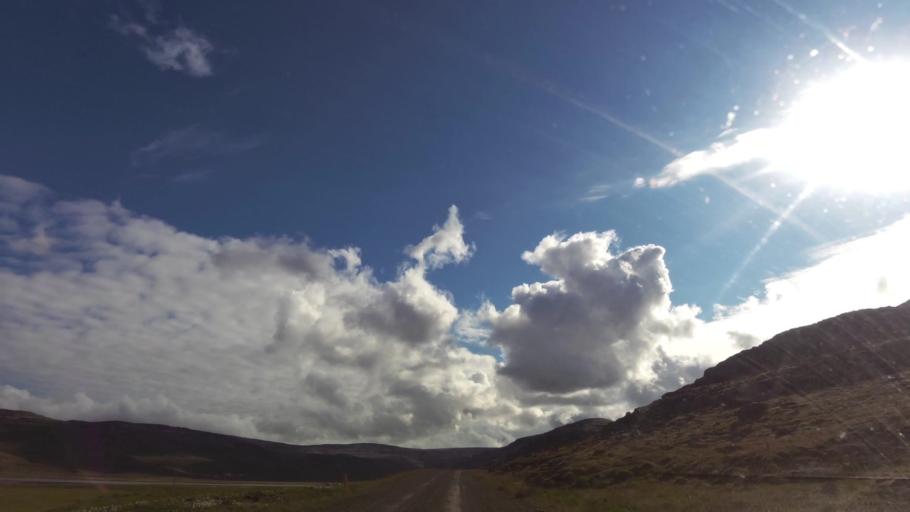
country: IS
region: West
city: Olafsvik
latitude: 65.5820
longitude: -24.1404
